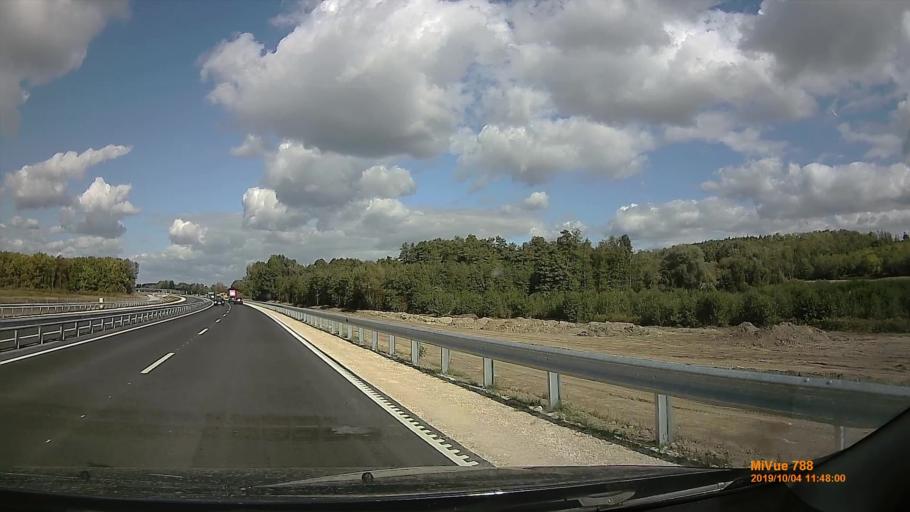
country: HU
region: Somogy
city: Karad
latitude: 46.6567
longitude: 17.7866
